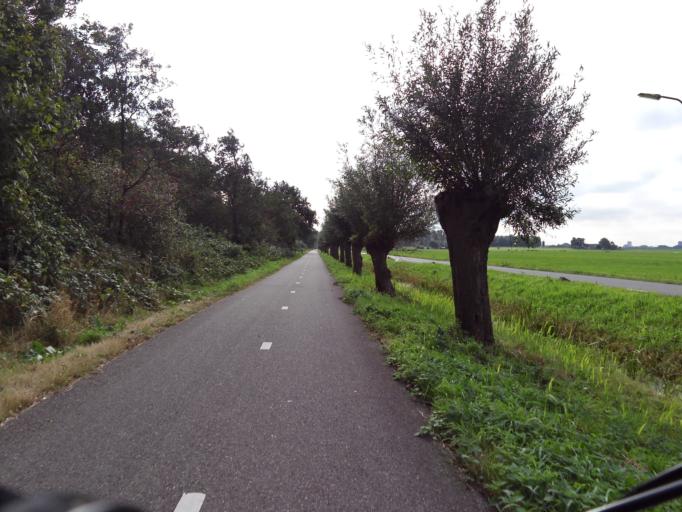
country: NL
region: South Holland
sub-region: Gemeente Zoetermeer
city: Zoetermeer
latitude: 52.0989
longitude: 4.5003
